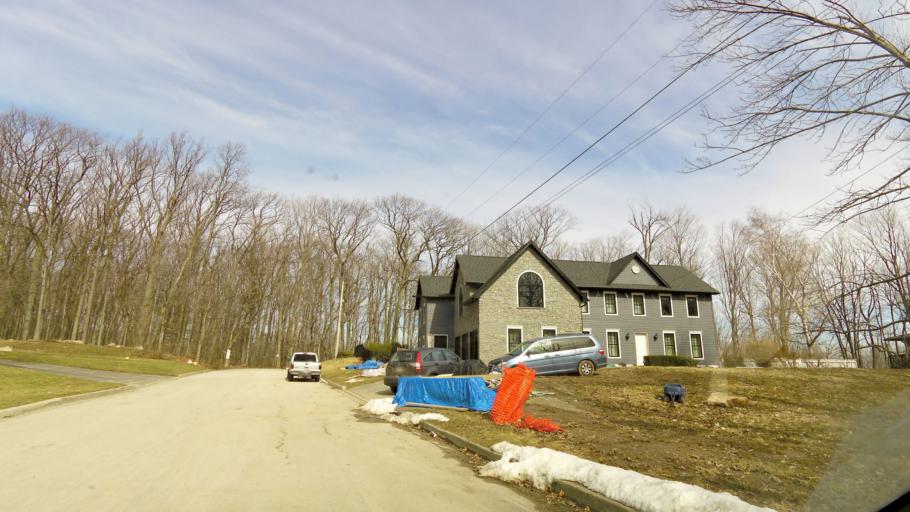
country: CA
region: Ontario
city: Burlington
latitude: 43.3708
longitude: -79.8594
